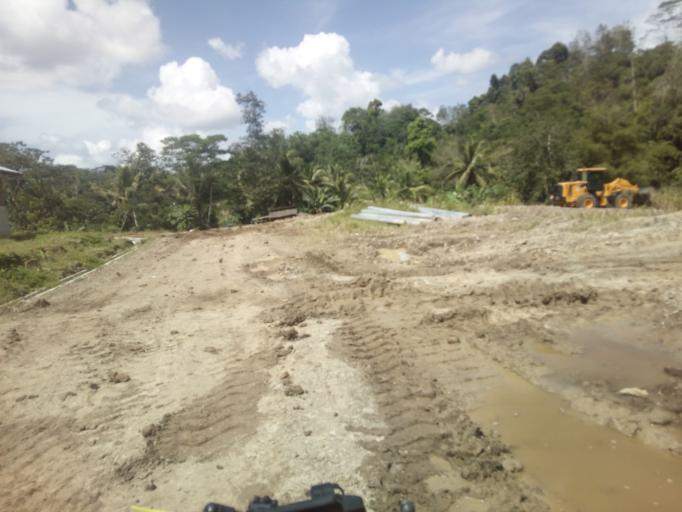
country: PH
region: Caraga
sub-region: Province of Agusan del Sur
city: Santa Josefa
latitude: 7.9835
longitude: 125.9709
